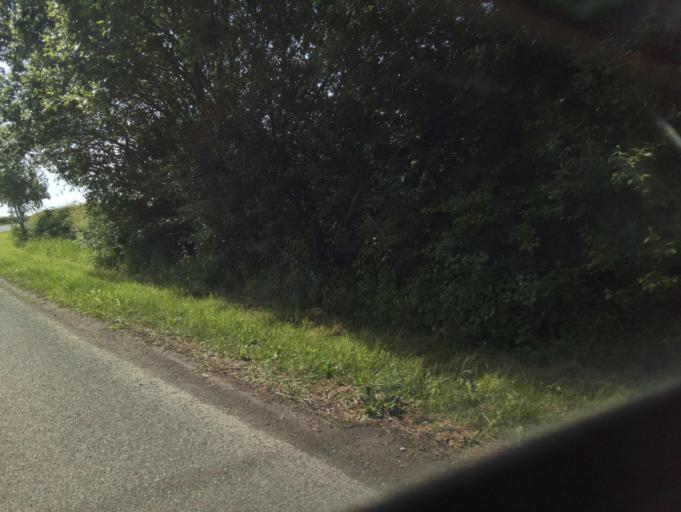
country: GB
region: England
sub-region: Lincolnshire
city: Skellingthorpe
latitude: 53.1653
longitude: -0.6396
